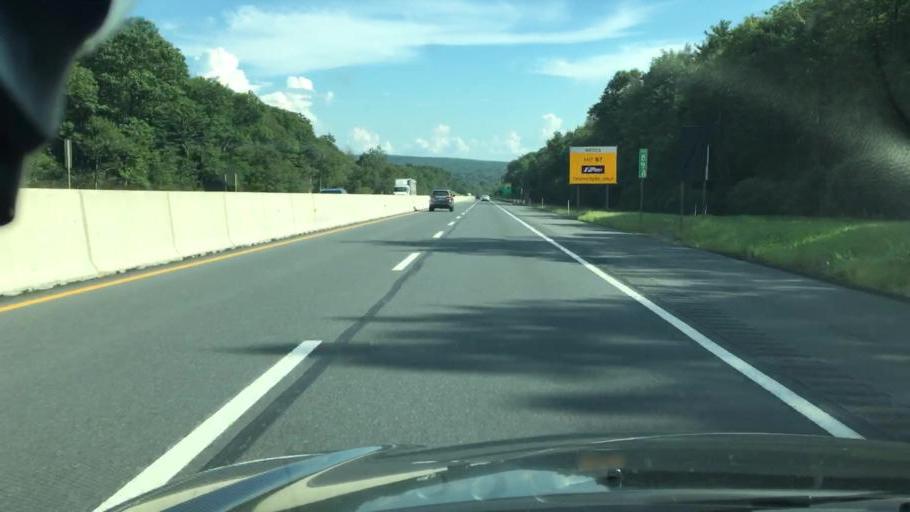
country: US
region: Pennsylvania
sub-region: Carbon County
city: Towamensing Trails
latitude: 41.0211
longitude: -75.6448
